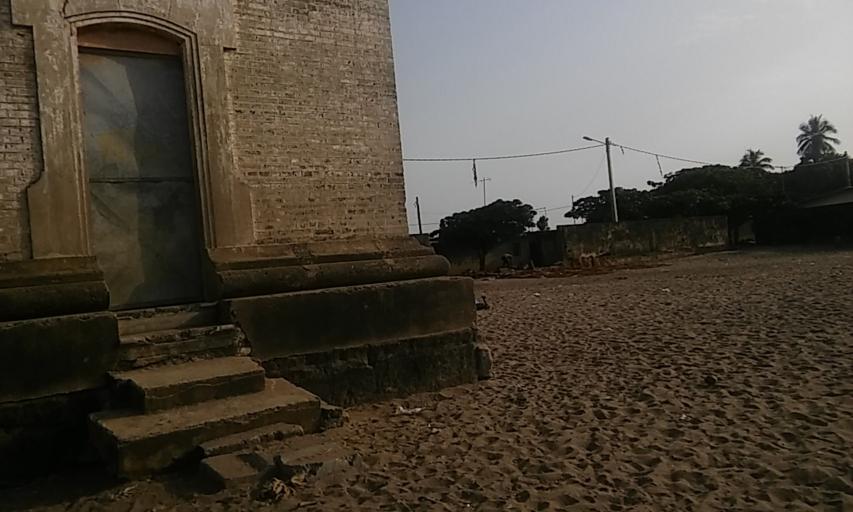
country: CI
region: Sud-Comoe
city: Grand-Bassam
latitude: 5.2051
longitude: -3.7316
